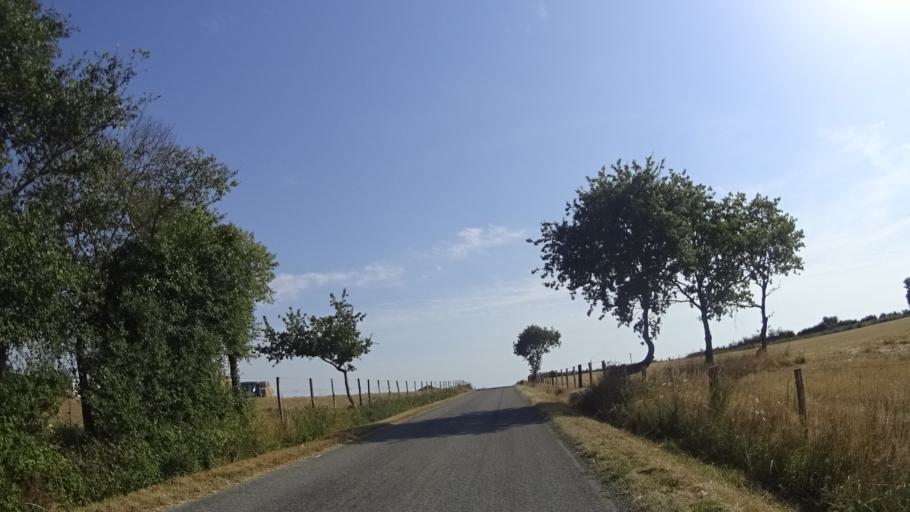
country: FR
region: Pays de la Loire
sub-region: Departement de la Loire-Atlantique
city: Donges
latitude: 47.3280
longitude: -2.0449
